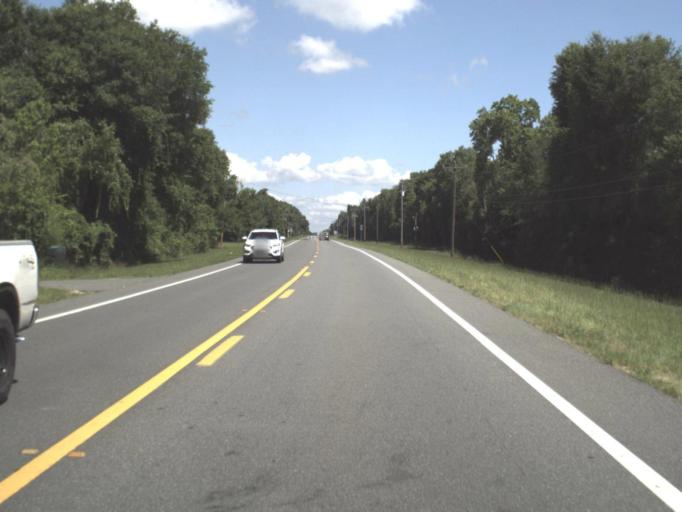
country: US
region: Florida
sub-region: Clay County
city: Keystone Heights
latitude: 29.7587
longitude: -81.9993
